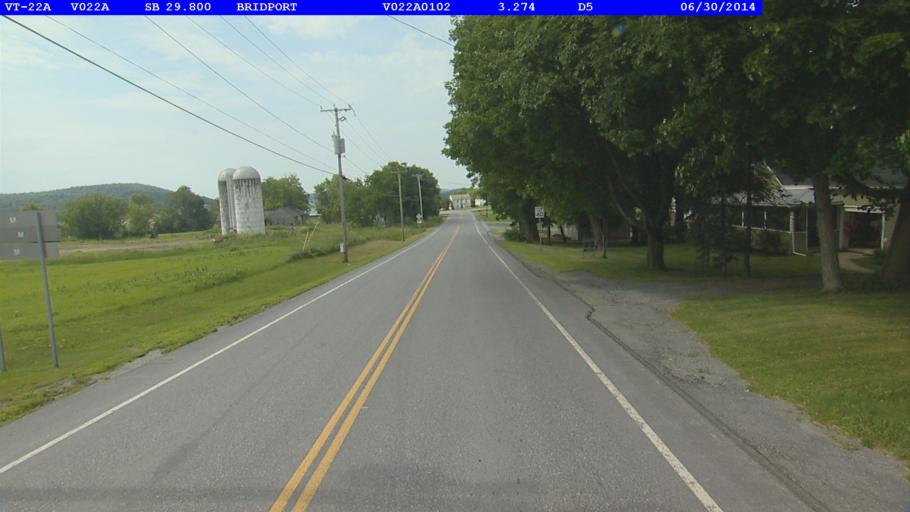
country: US
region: Vermont
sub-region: Addison County
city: Middlebury (village)
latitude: 43.9874
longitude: -73.3130
